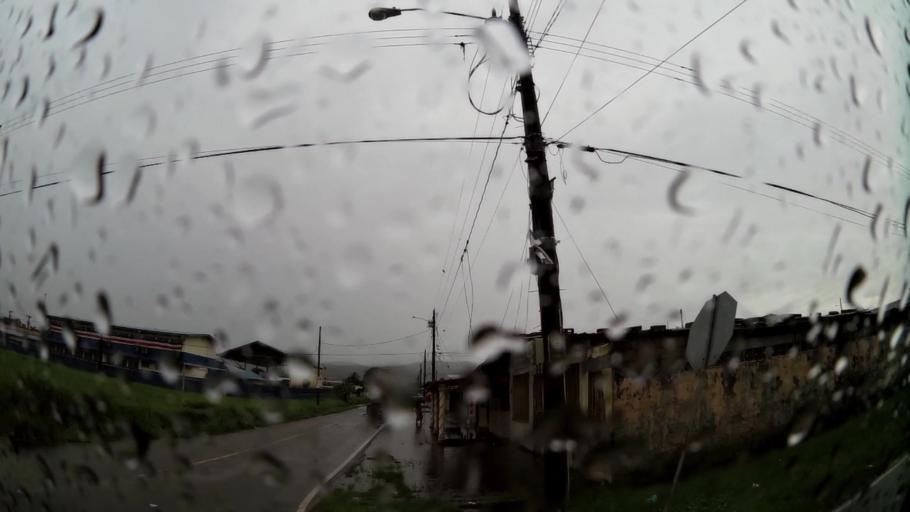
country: PA
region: Colon
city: Sabanitas
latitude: 9.3544
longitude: -79.8080
